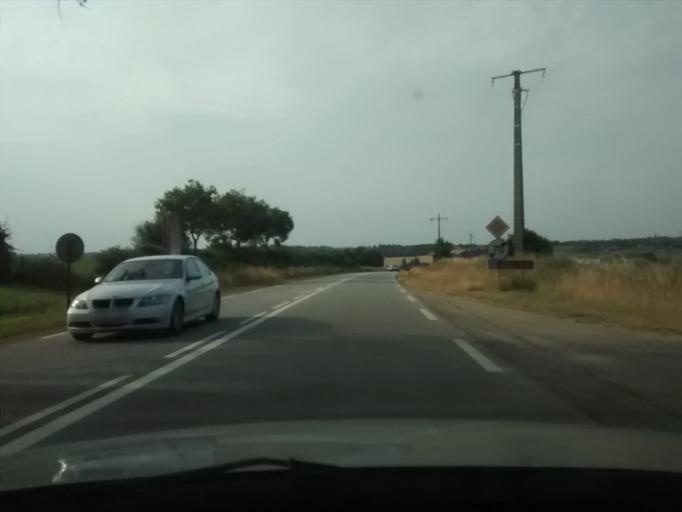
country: FR
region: Brittany
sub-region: Departement d'Ille-et-Vilaine
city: Etrelles
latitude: 48.0744
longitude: -1.2001
